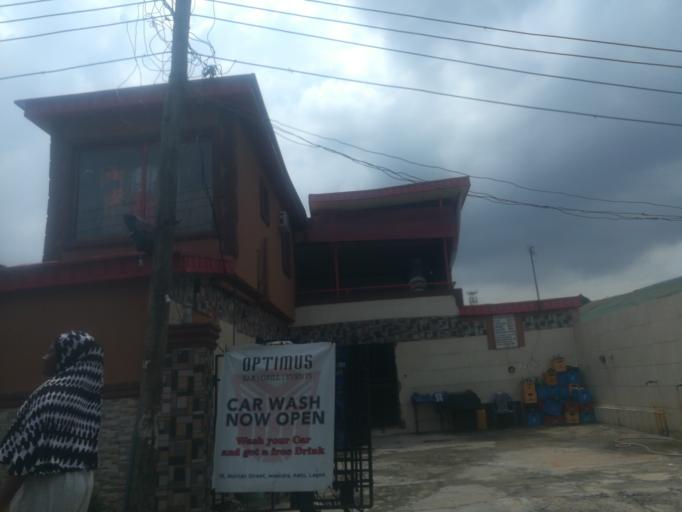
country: NG
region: Lagos
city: Ojota
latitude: 6.5957
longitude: 3.3898
